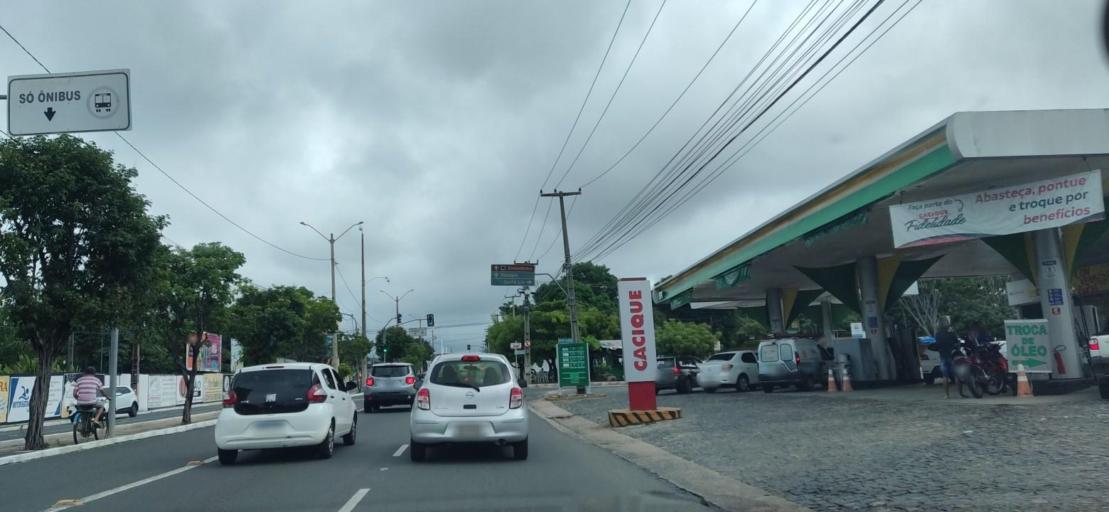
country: BR
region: Piaui
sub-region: Teresina
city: Teresina
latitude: -5.0655
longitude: -42.7701
